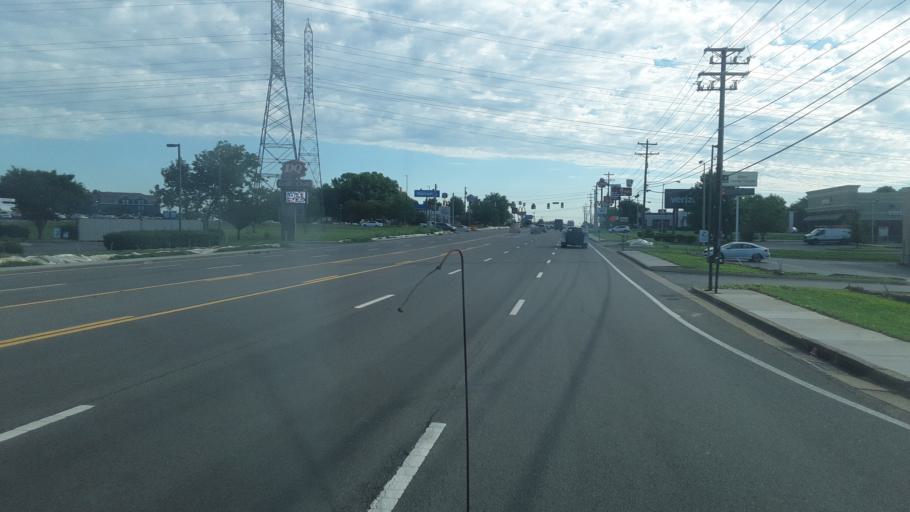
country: US
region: Tennessee
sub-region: Montgomery County
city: Clarksville
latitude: 36.5919
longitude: -87.2904
